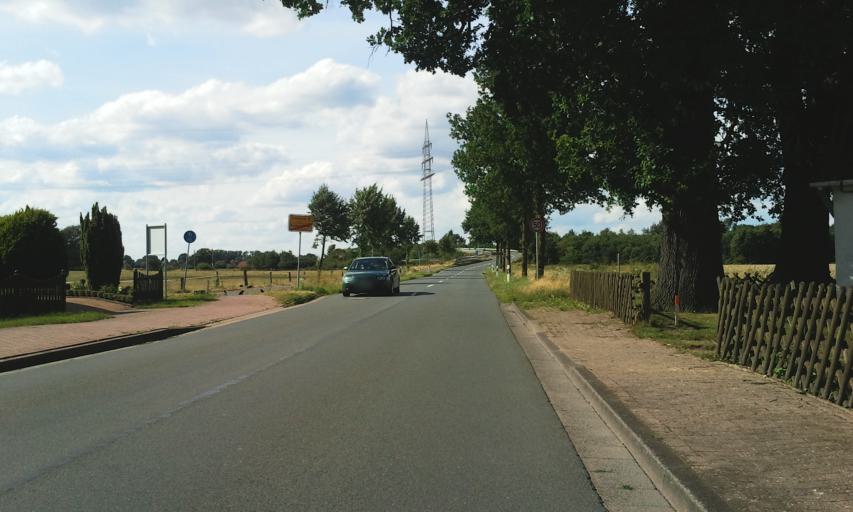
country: DE
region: Lower Saxony
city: Drakenburg
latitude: 52.6788
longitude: 9.2245
